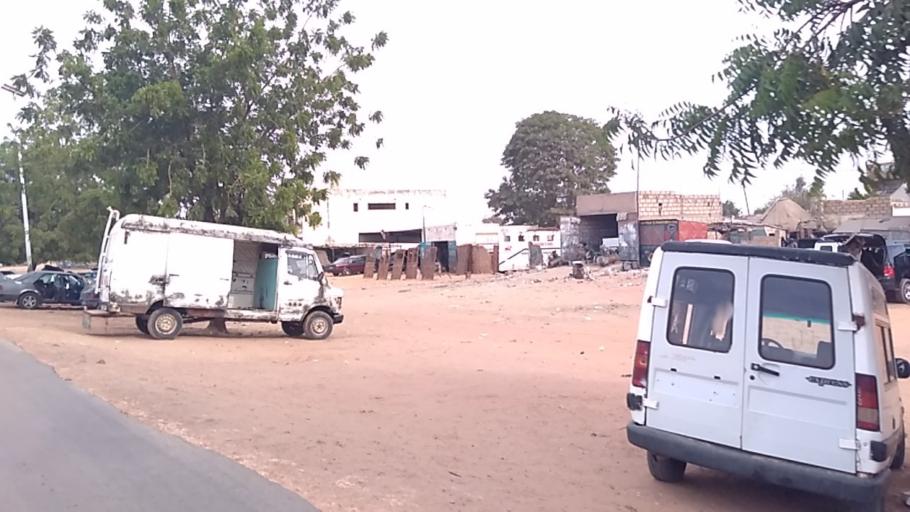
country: SN
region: Diourbel
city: Touba
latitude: 14.8424
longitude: -15.8675
